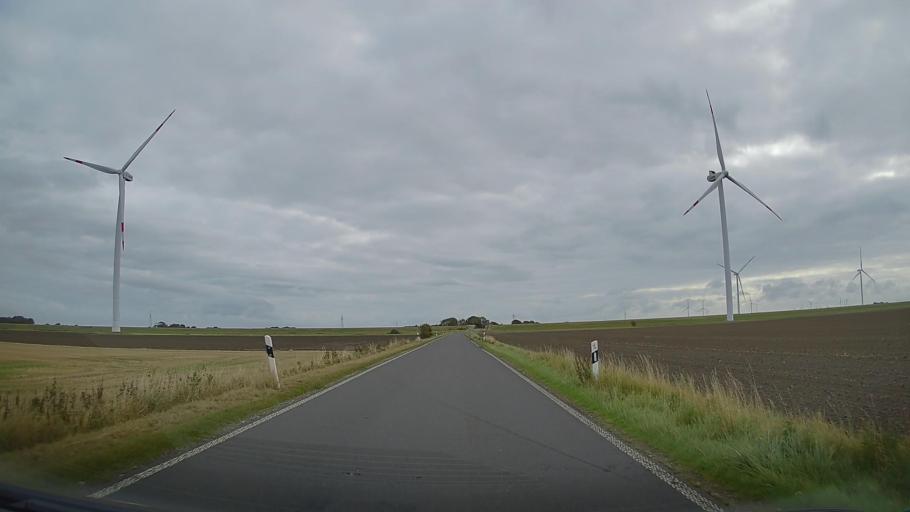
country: DE
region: Schleswig-Holstein
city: Friedrich-Wilhelm-Lubke-Koog
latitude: 54.8687
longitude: 8.6395
